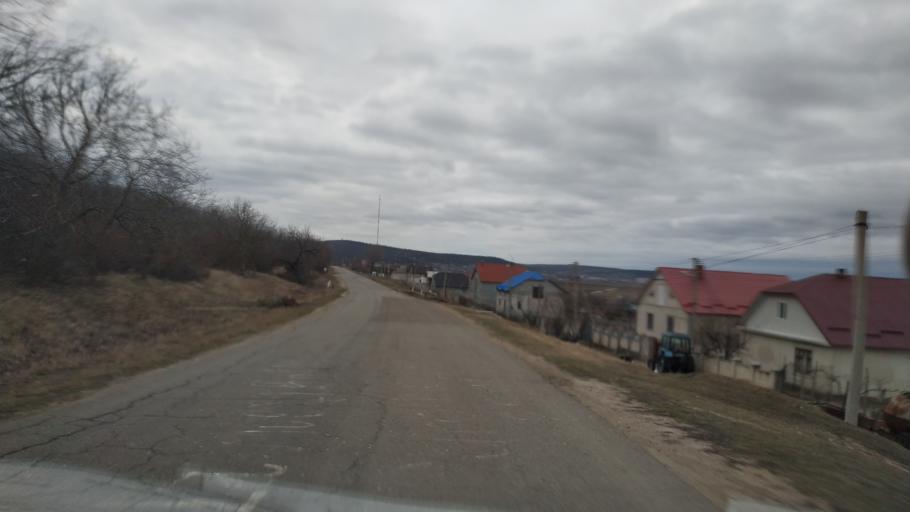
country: MD
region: Causeni
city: Causeni
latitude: 46.6627
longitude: 29.4493
